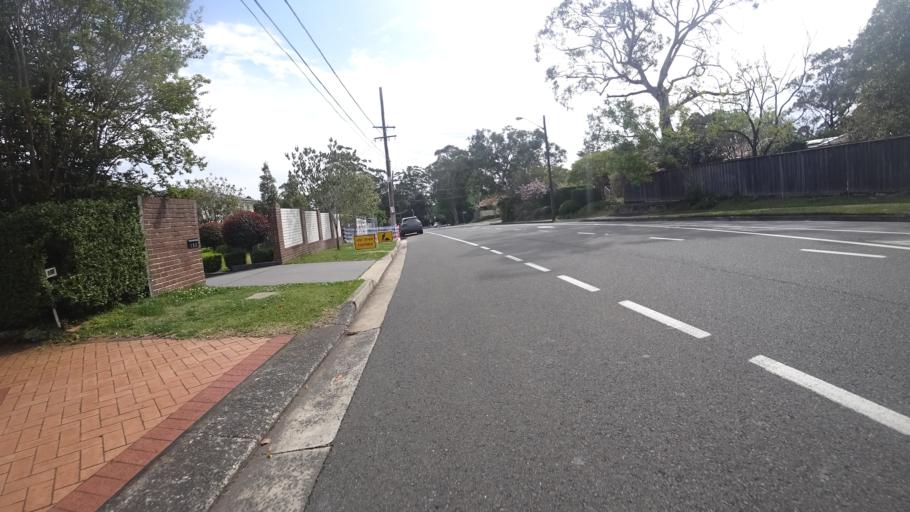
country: AU
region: New South Wales
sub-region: City of Sydney
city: North Turramurra
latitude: -33.7211
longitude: 151.1424
